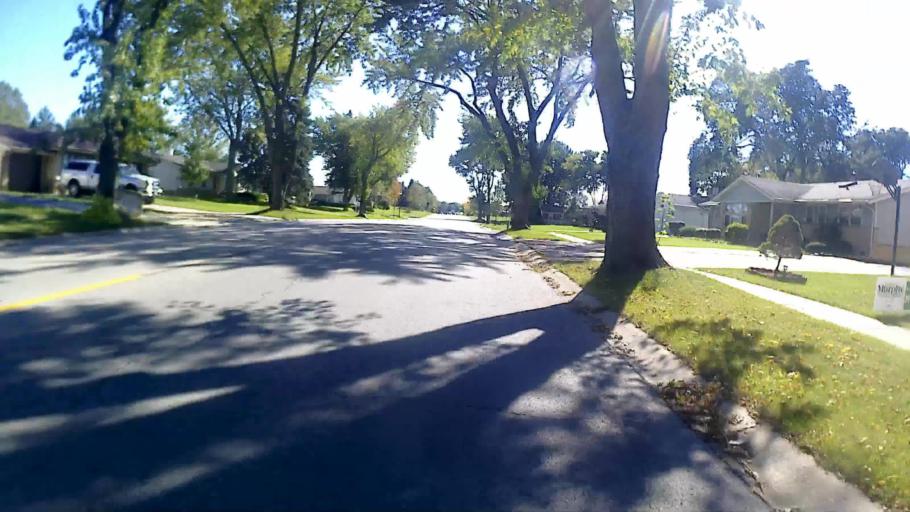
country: US
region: Illinois
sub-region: Cook County
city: Elk Grove Village
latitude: 41.9960
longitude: -87.9892
